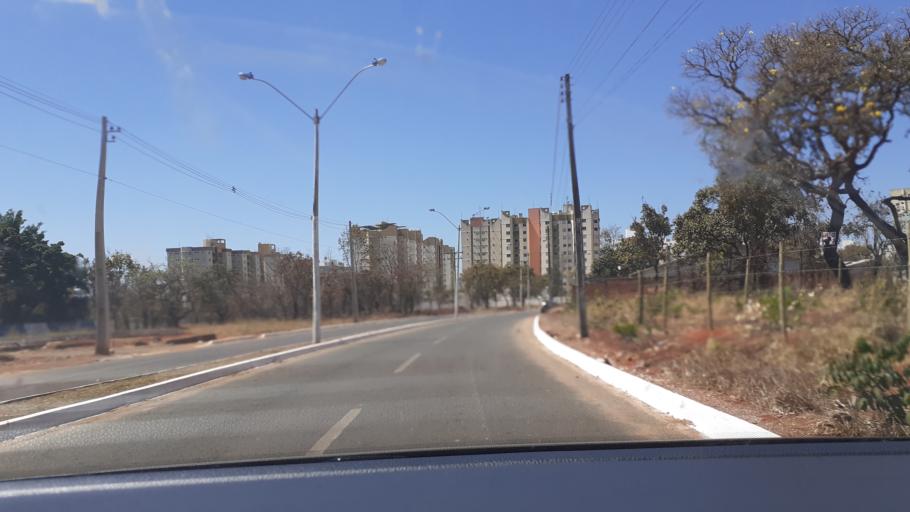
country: BR
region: Goias
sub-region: Caldas Novas
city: Caldas Novas
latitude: -17.7383
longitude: -48.6382
